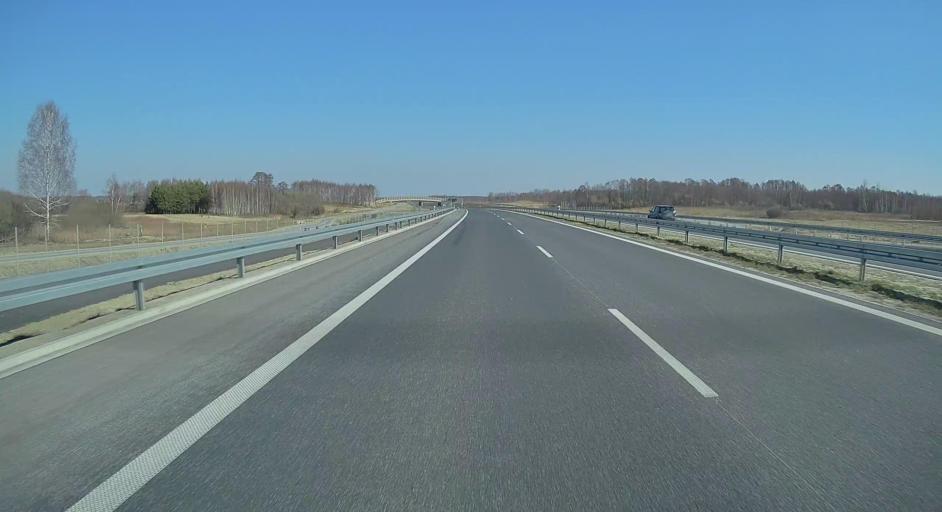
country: PL
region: Subcarpathian Voivodeship
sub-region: Powiat rzeszowski
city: Gorno
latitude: 50.3165
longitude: 22.1716
